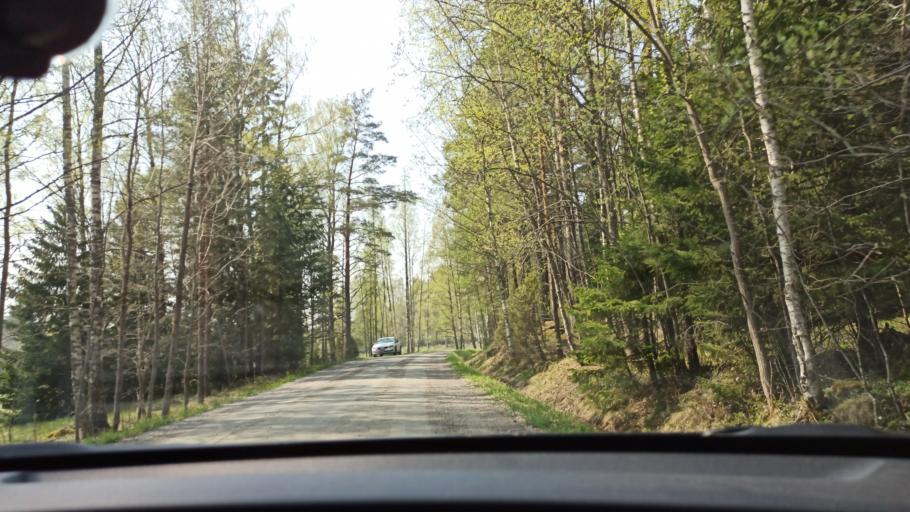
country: FI
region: Uusimaa
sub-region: Helsinki
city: Espoo
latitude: 60.0886
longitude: 24.5910
